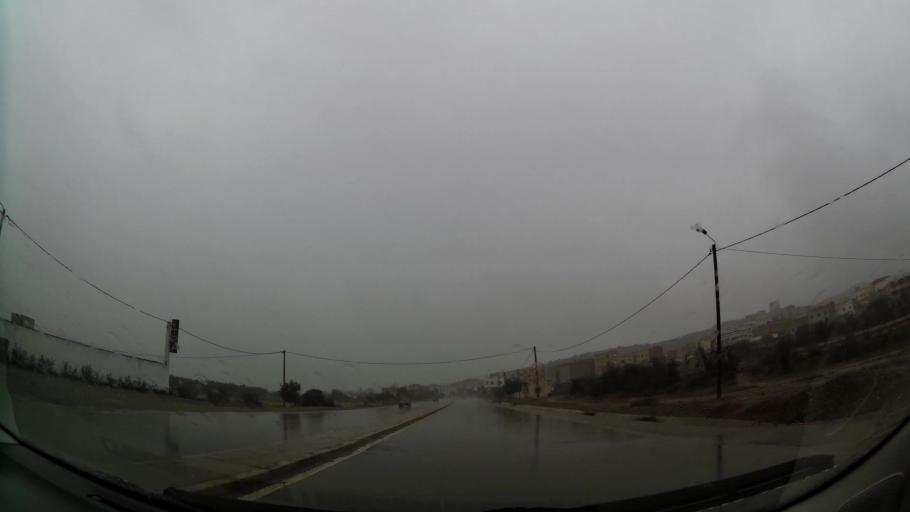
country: MA
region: Taza-Al Hoceima-Taounate
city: Imzourene
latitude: 35.1282
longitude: -3.8460
